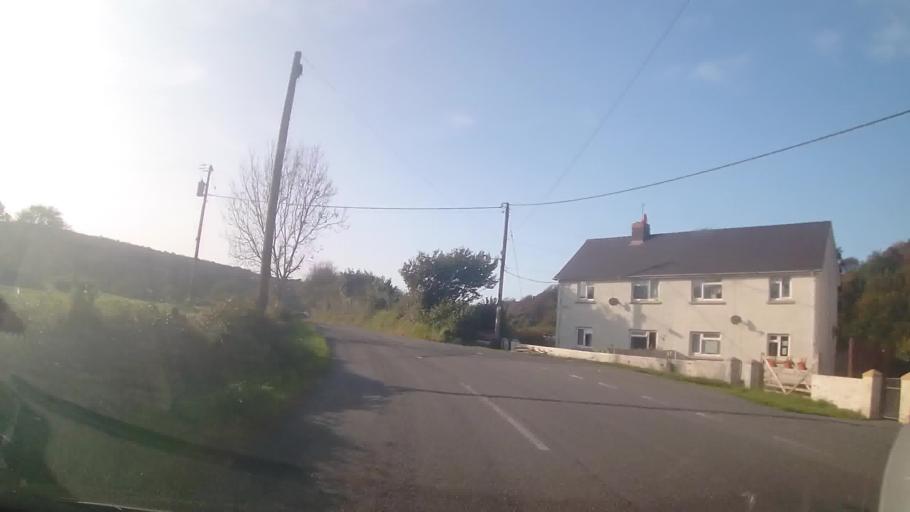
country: GB
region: Wales
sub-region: Pembrokeshire
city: Fishguard
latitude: 51.9788
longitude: -4.9279
